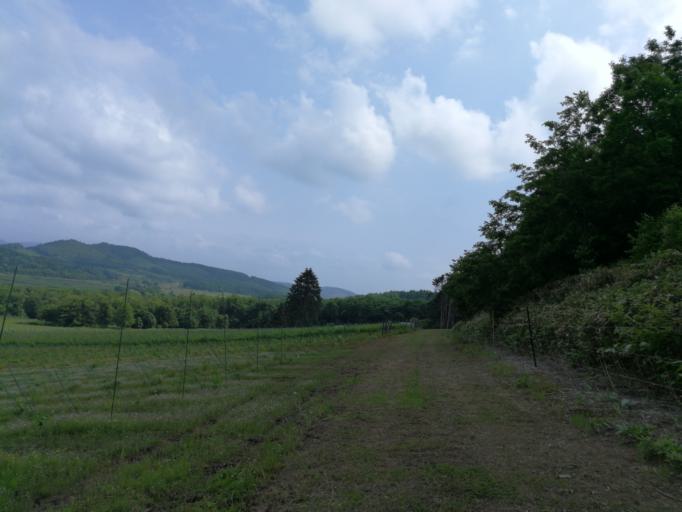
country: JP
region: Hokkaido
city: Iwamizawa
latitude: 43.1923
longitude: 141.8174
